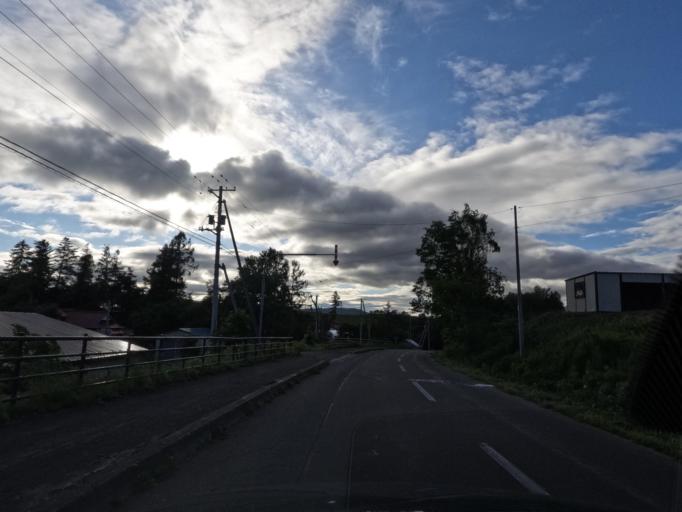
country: JP
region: Hokkaido
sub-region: Asahikawa-shi
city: Asahikawa
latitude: 43.6311
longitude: 142.4357
